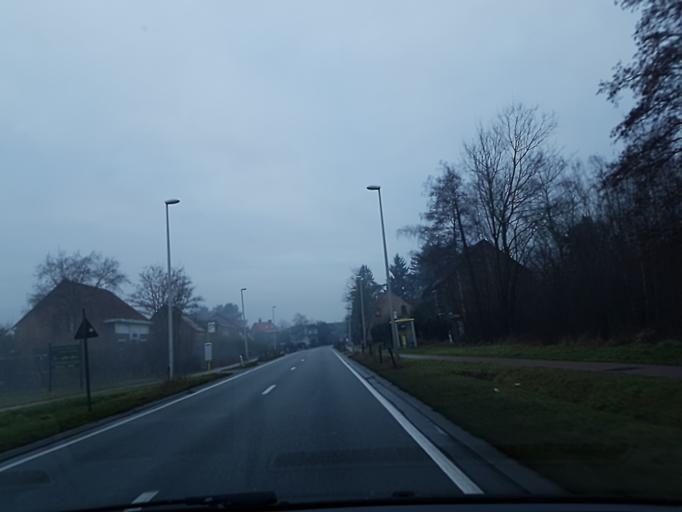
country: BE
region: Flanders
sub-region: Provincie Antwerpen
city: Lier
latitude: 51.1389
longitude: 4.6125
